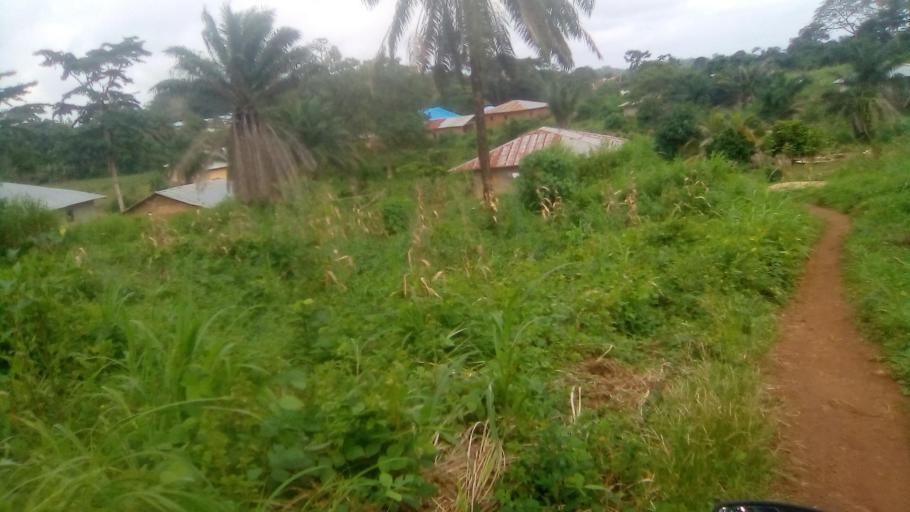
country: SL
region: Eastern Province
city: Kailahun
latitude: 8.2686
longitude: -10.5595
